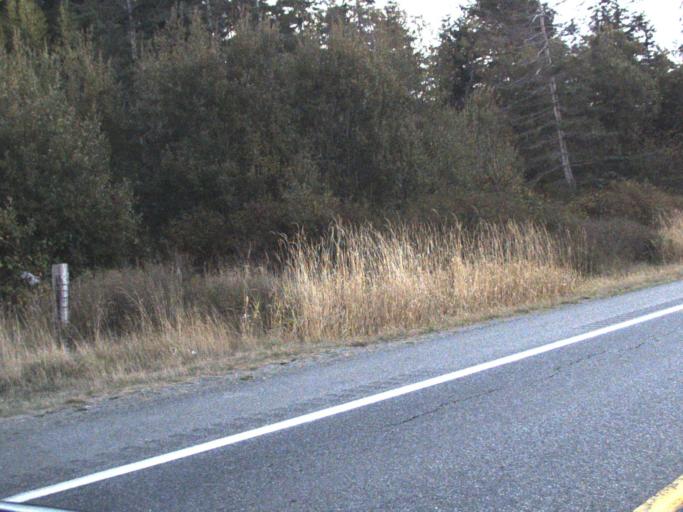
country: US
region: Washington
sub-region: Island County
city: Oak Harbor
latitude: 48.2685
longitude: -122.6718
